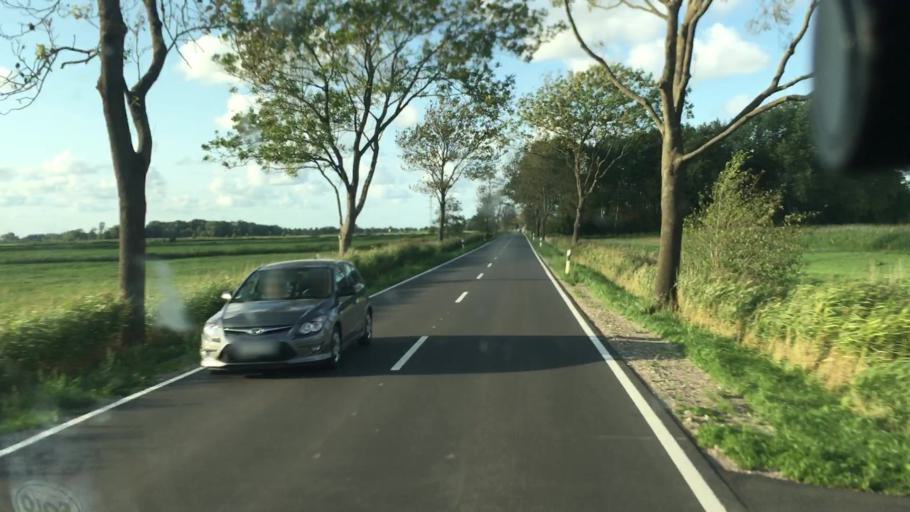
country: DE
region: Lower Saxony
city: Jever
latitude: 53.6309
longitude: 7.8615
